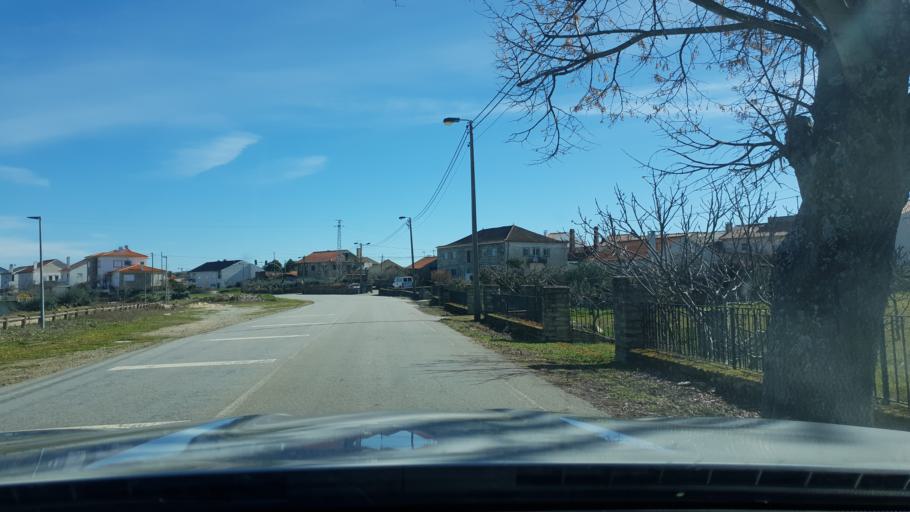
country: PT
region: Braganca
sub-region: Freixo de Espada A Cinta
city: Freixo de Espada a Cinta
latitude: 41.1817
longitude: -6.8918
